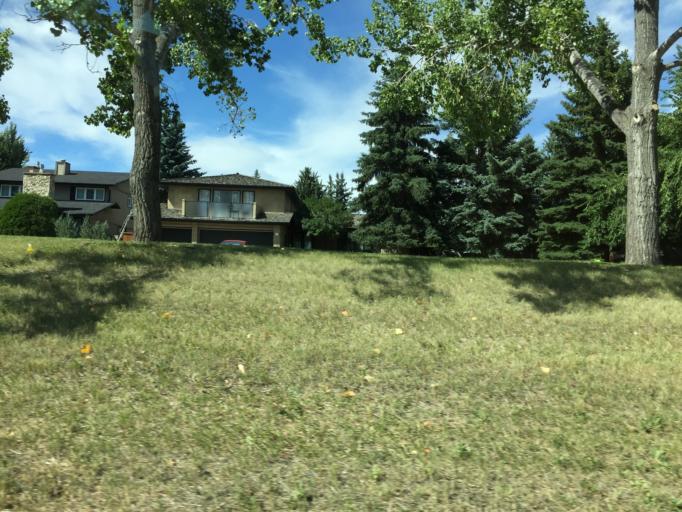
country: CA
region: Alberta
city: Calgary
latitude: 50.9307
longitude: -114.0553
